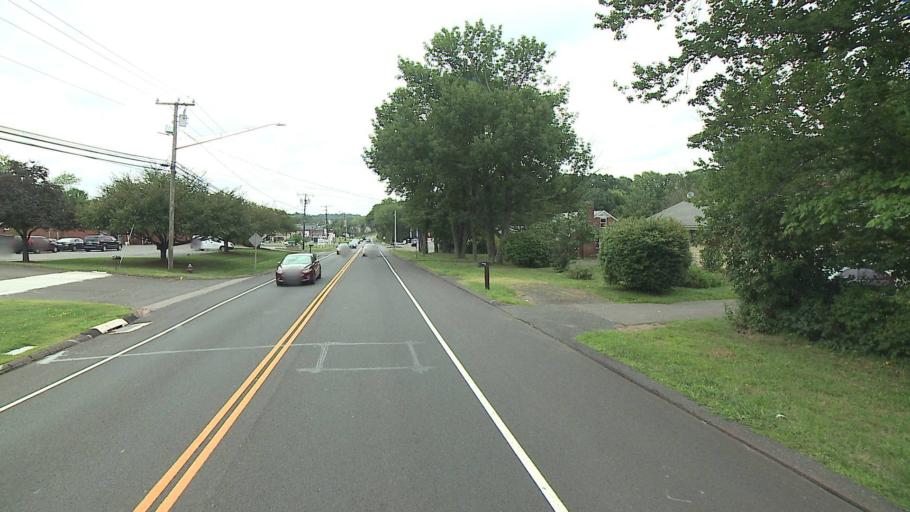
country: US
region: Connecticut
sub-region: Middlesex County
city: Cromwell
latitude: 41.6251
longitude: -72.6759
